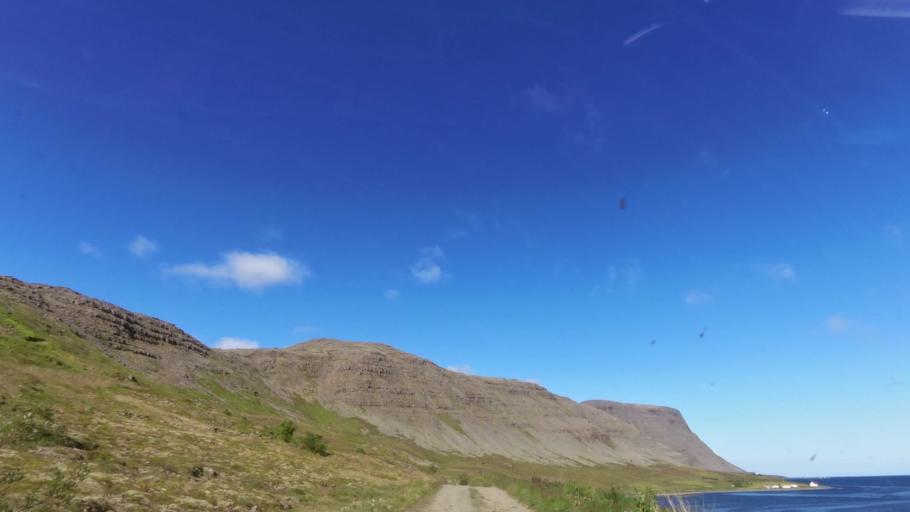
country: IS
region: West
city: Olafsvik
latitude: 65.6170
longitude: -23.8524
